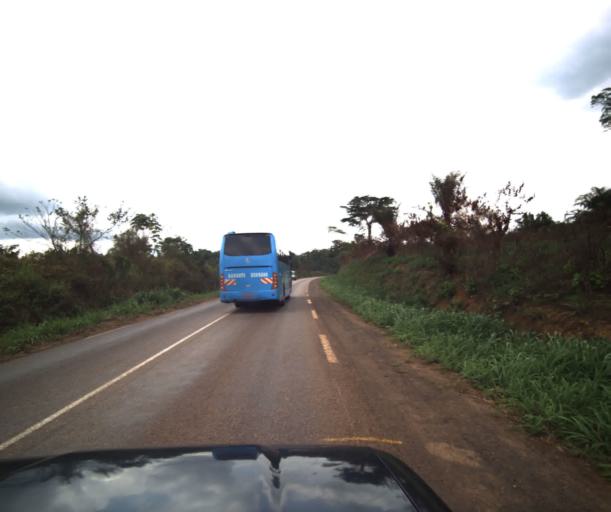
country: CM
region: Centre
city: Eseka
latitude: 3.8694
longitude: 10.6532
